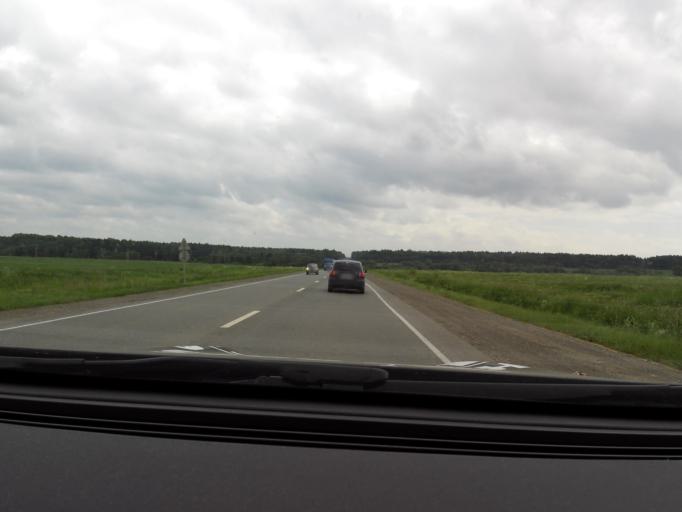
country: RU
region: Perm
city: Kukushtan
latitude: 57.6094
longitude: 56.5045
